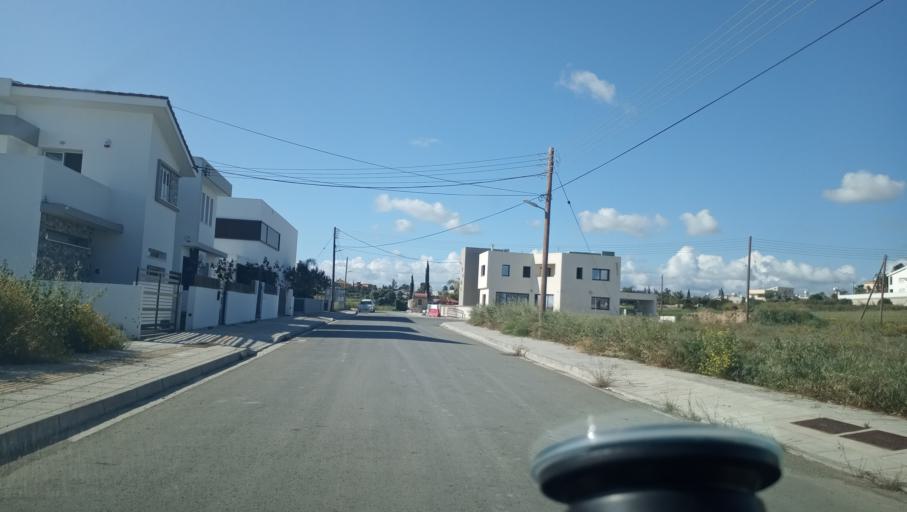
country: CY
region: Lefkosia
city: Geri
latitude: 35.1040
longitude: 33.3946
